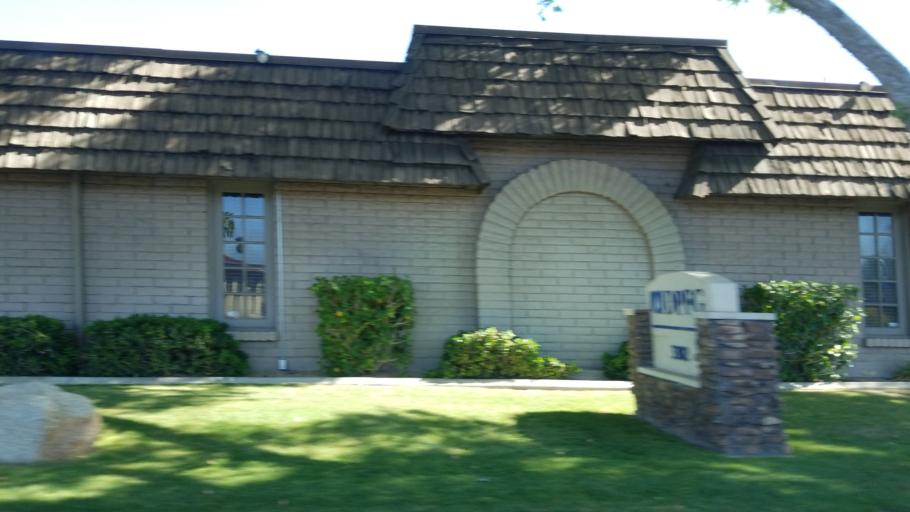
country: US
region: Arizona
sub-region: Maricopa County
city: Paradise Valley
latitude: 33.4953
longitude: -112.0098
